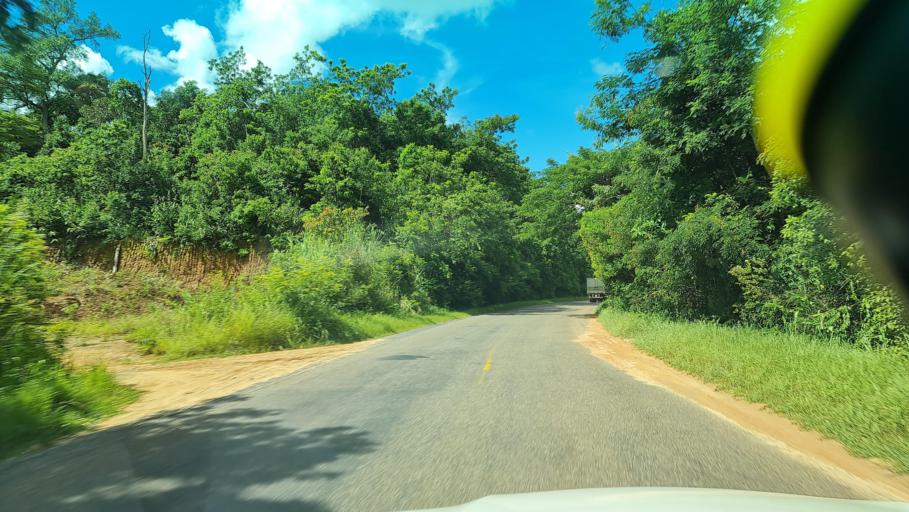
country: LA
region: Bolikhamxai
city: Pakkading
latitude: 18.2876
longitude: 104.0752
